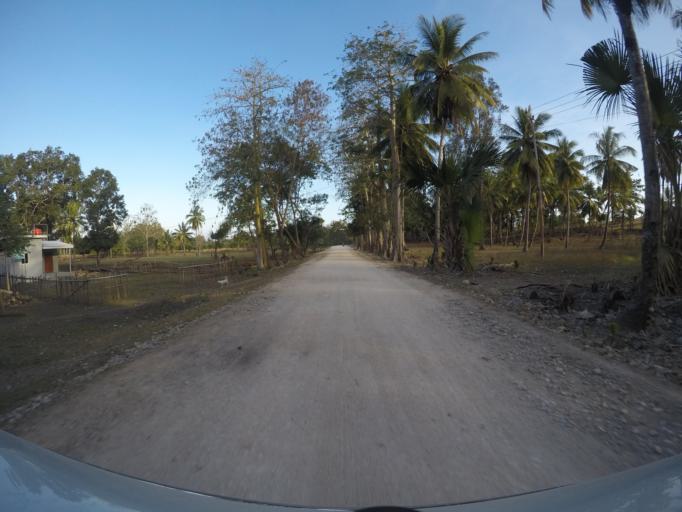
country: TL
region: Viqueque
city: Viqueque
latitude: -8.8743
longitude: 126.5075
